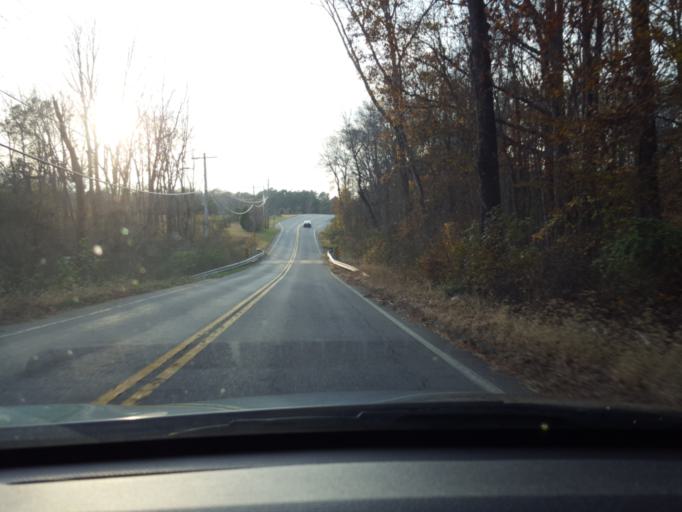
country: US
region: Maryland
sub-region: Charles County
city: Hughesville
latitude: 38.5294
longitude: -76.8016
